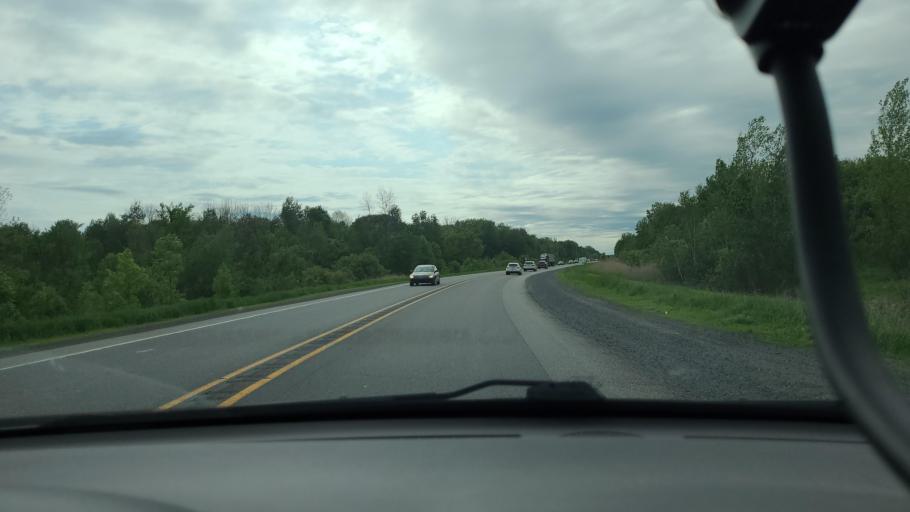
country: CA
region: Quebec
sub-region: Lanaudiere
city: Saint-Jacques
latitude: 45.9730
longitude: -73.5430
